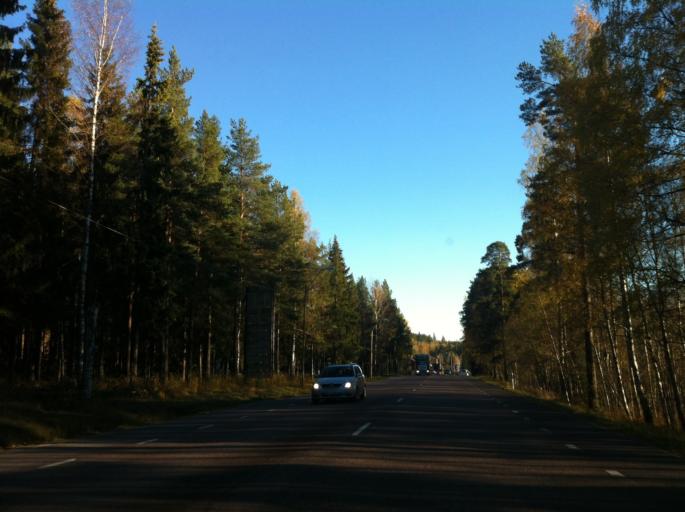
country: SE
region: Dalarna
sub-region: Faluns Kommun
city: Grycksbo
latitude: 60.6857
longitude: 15.4978
